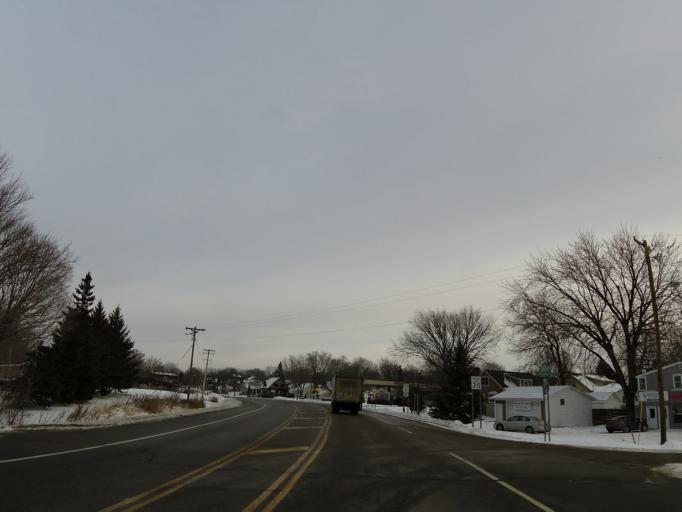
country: US
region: Minnesota
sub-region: Carver County
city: Victoria
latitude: 44.8592
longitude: -93.6647
